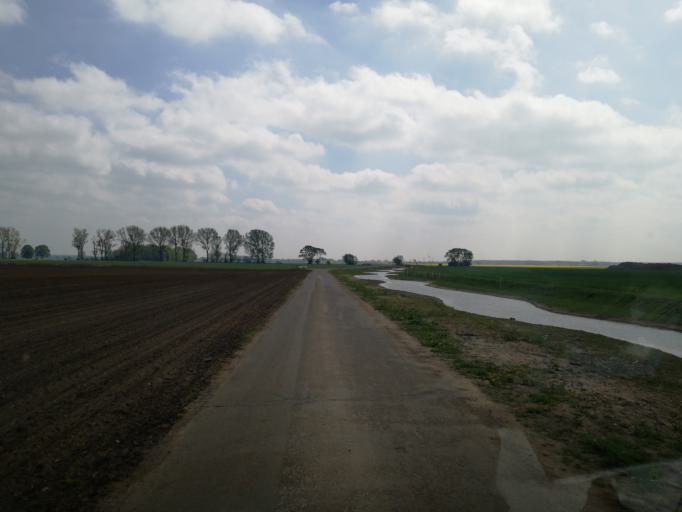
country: DE
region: Brandenburg
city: Doberlug-Kirchhain
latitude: 51.6796
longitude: 13.5356
